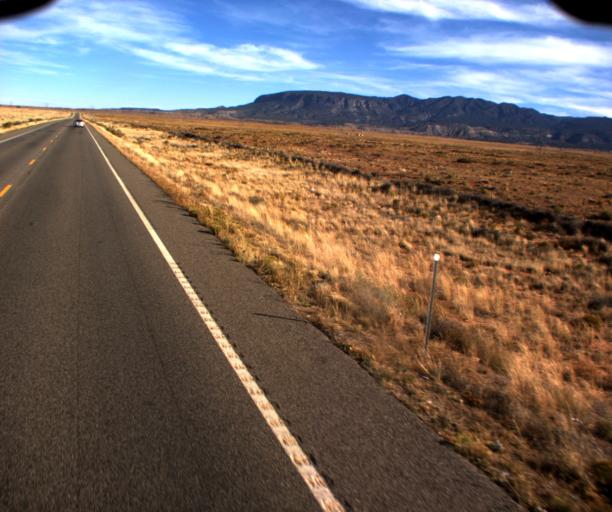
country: US
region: Arizona
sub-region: Apache County
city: Lukachukai
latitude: 36.9438
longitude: -109.2615
